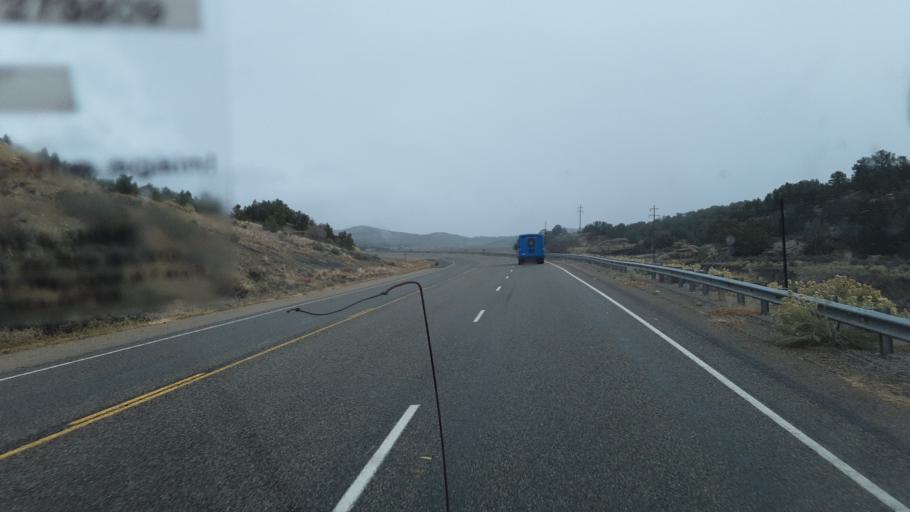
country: US
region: New Mexico
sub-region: Rio Arriba County
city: Tierra Amarilla
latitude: 36.4344
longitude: -106.4751
